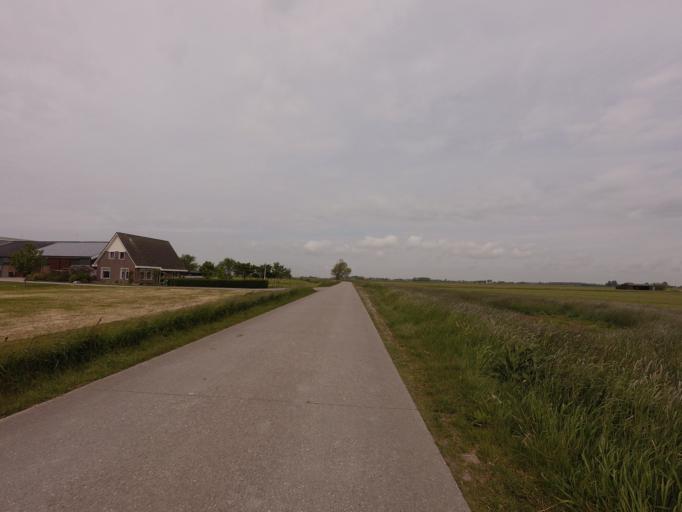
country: NL
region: Friesland
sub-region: Sudwest Fryslan
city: Makkum
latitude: 53.0646
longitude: 5.4603
